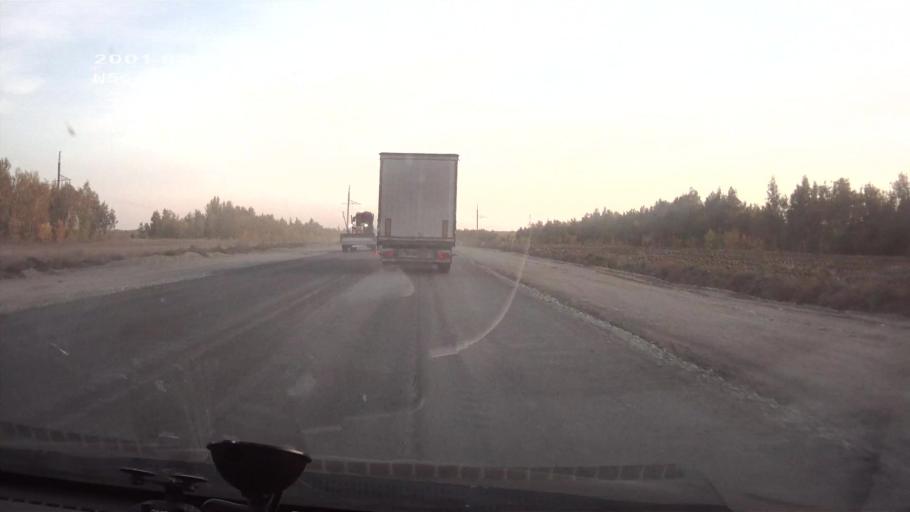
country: RU
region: Saratov
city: Kamenskiy
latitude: 50.9247
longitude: 45.5988
